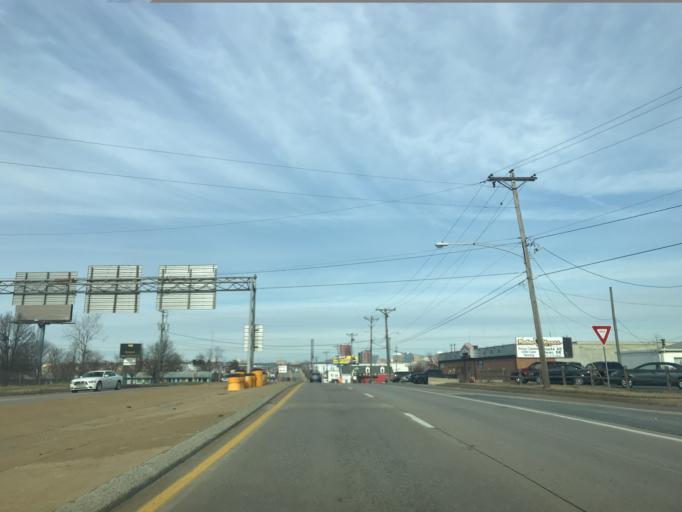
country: US
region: Delaware
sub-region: New Castle County
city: Wilmington
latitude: 39.7198
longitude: -75.5556
